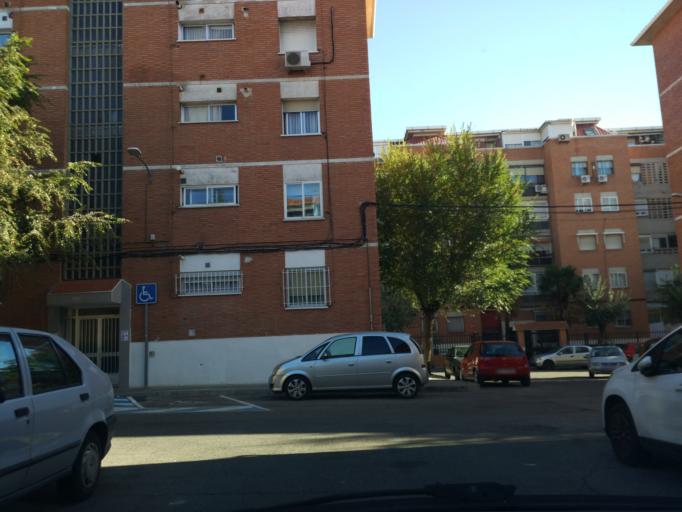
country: ES
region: Madrid
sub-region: Provincia de Madrid
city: Torrejon de Ardoz
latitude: 40.4528
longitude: -3.4692
